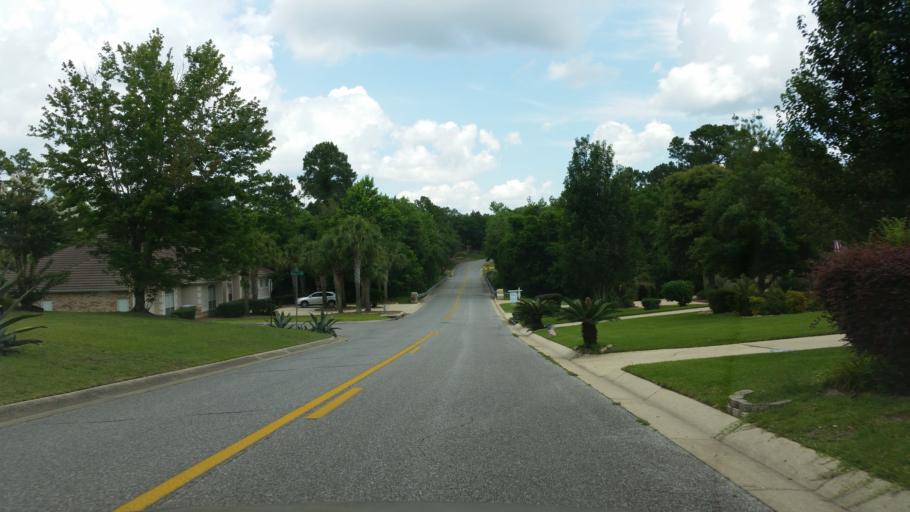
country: US
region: Florida
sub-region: Escambia County
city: Bellview
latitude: 30.4783
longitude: -87.2849
